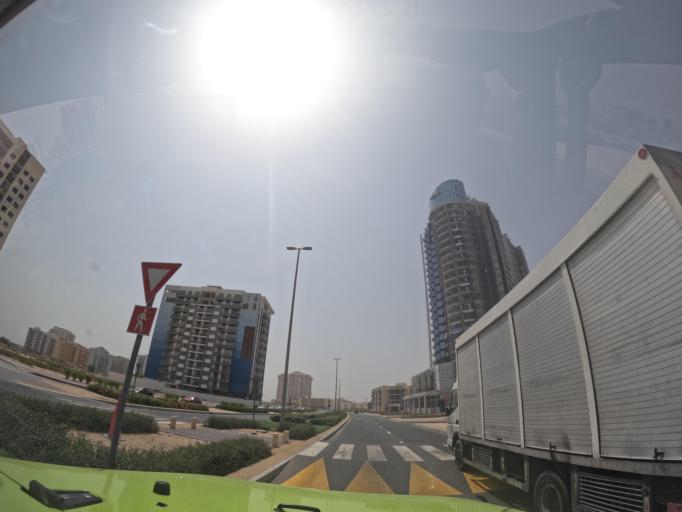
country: AE
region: Dubai
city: Dubai
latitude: 25.0979
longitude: 55.3788
